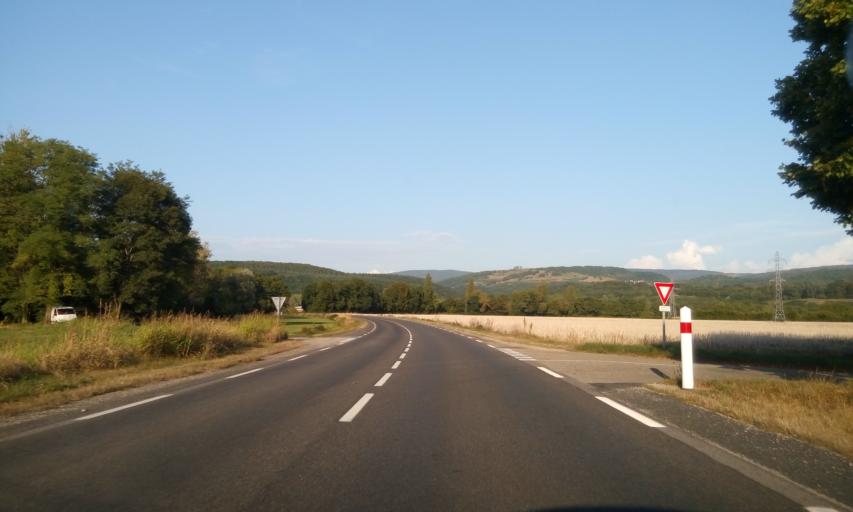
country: FR
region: Rhone-Alpes
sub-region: Departement de l'Ain
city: Saint-Jean-le-Vieux
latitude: 46.0450
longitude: 5.3753
